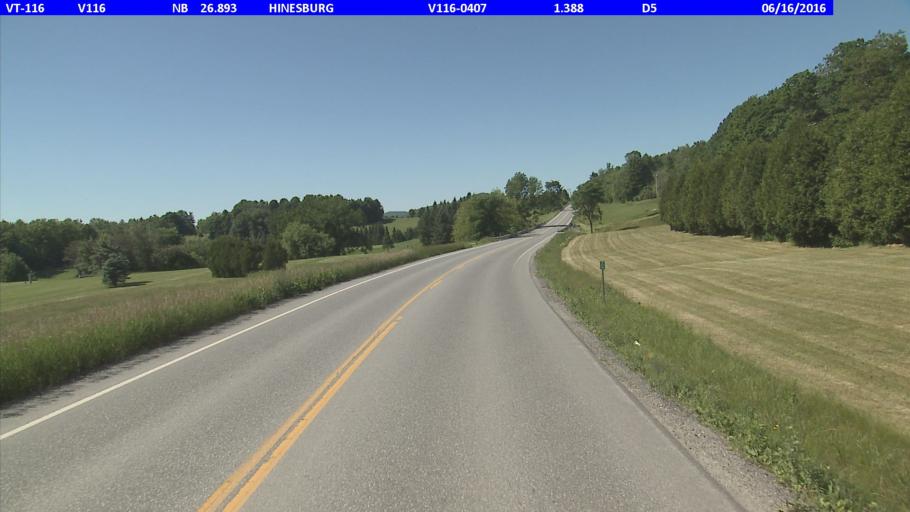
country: US
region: Vermont
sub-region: Chittenden County
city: Hinesburg
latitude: 44.2996
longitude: -73.0739
